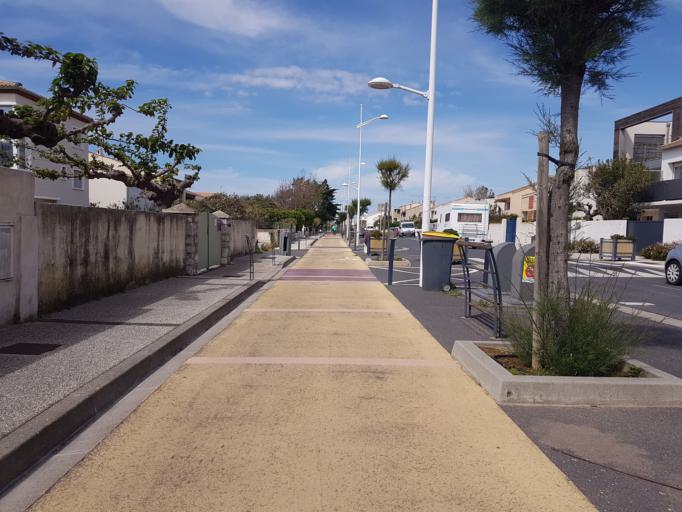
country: FR
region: Languedoc-Roussillon
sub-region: Departement de l'Herault
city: Perols
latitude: 43.5501
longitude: 3.9976
